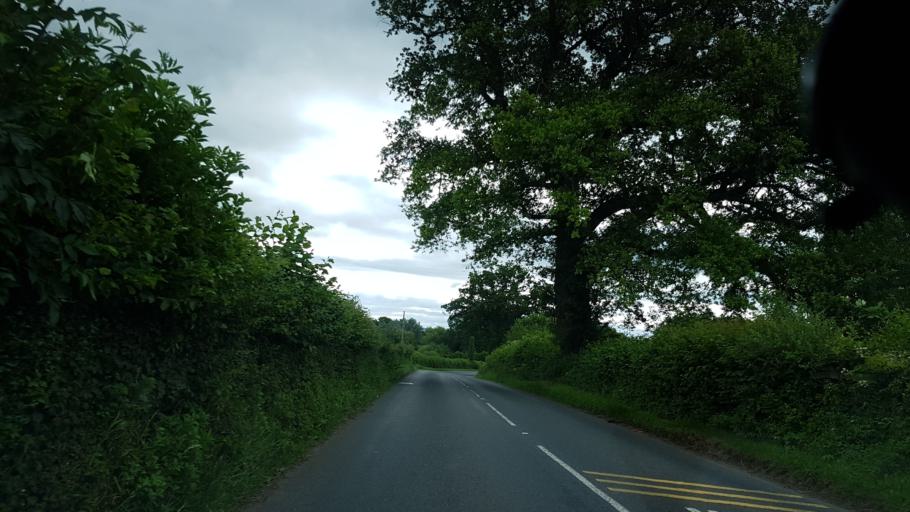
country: GB
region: Wales
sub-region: Monmouthshire
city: Llanarth
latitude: 51.7747
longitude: -2.8851
